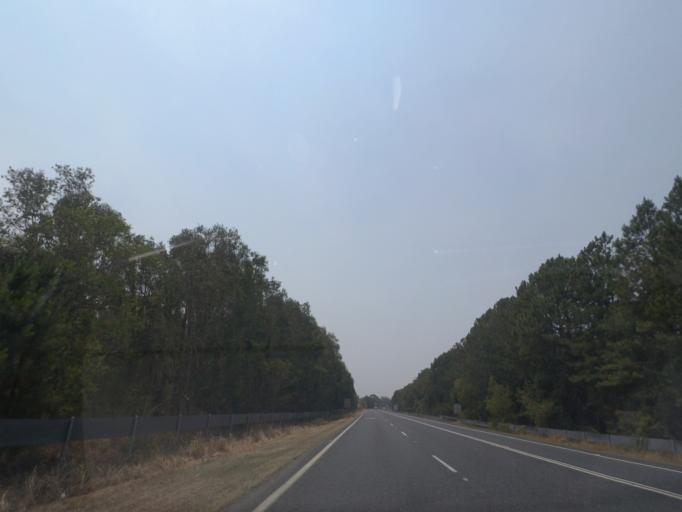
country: AU
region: New South Wales
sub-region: Ballina
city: Ballina
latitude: -28.9394
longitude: 153.4699
